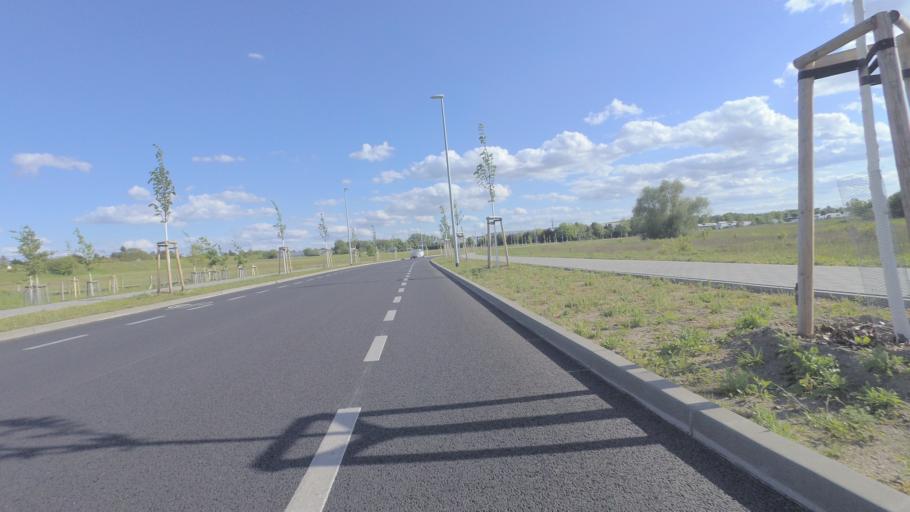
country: DE
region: Brandenburg
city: Teltow
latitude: 52.3913
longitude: 13.2418
